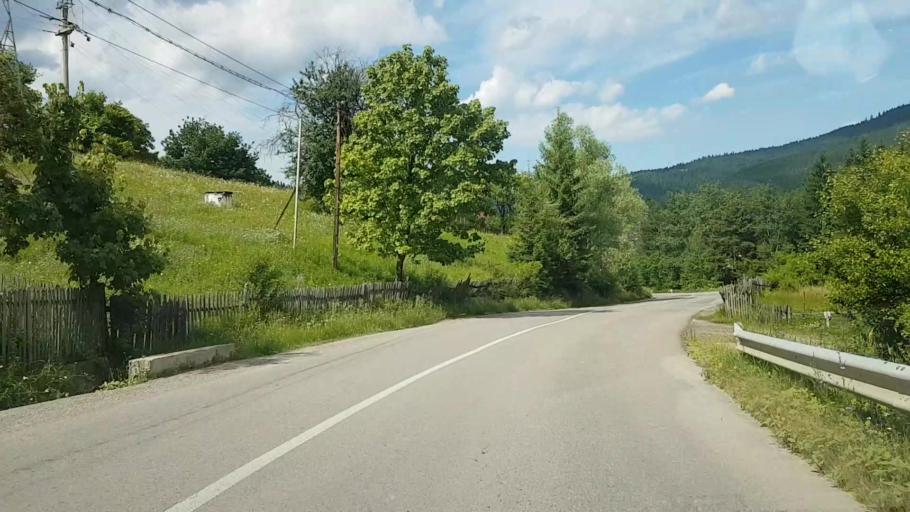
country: RO
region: Neamt
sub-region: Comuna Hangu
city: Hangu
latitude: 47.0573
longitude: 26.0309
